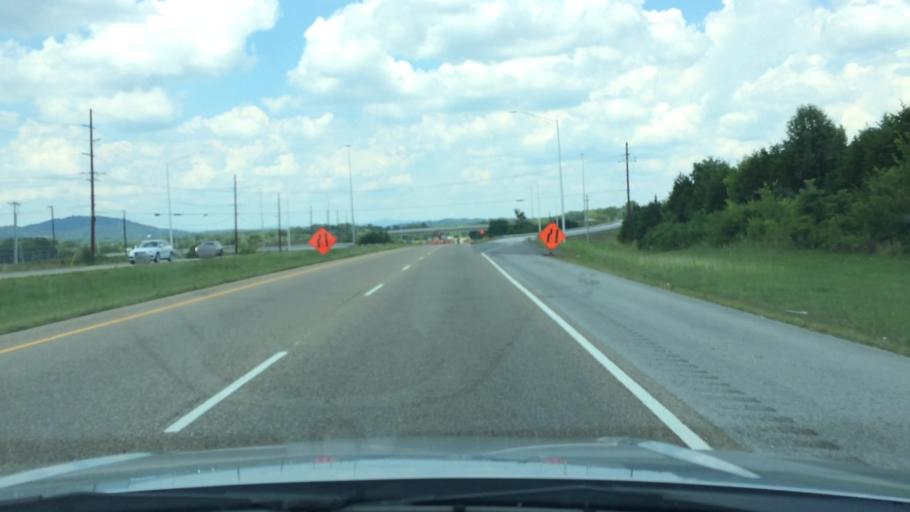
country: US
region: Tennessee
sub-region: Hamblen County
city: Morristown
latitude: 36.1715
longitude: -83.3505
